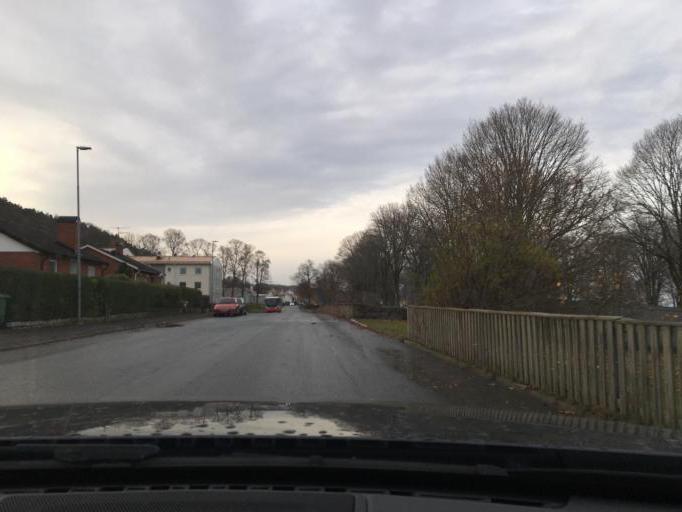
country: SE
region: Joenkoeping
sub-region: Jonkopings Kommun
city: Graenna
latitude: 58.0205
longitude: 14.4615
